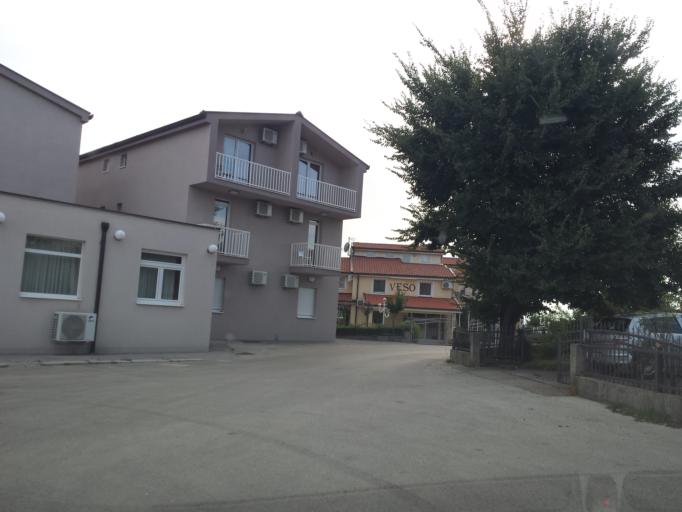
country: BA
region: Federation of Bosnia and Herzegovina
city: Citluk
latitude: 43.1984
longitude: 17.6722
